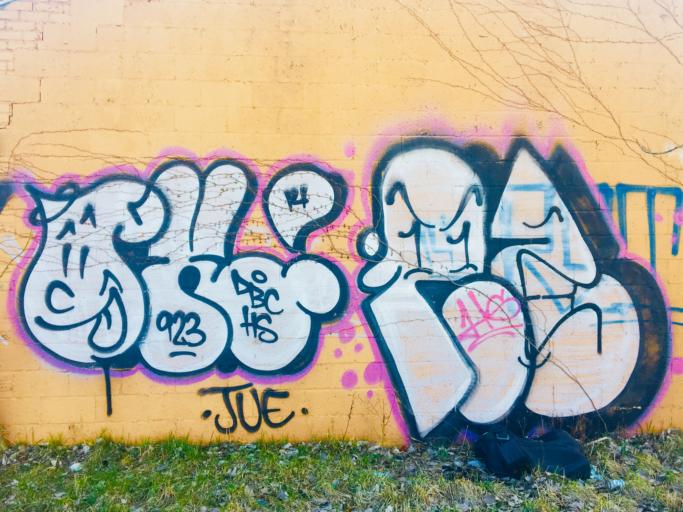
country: US
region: Michigan
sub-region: Wayne County
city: Dearborn
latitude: 42.3660
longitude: -83.1635
